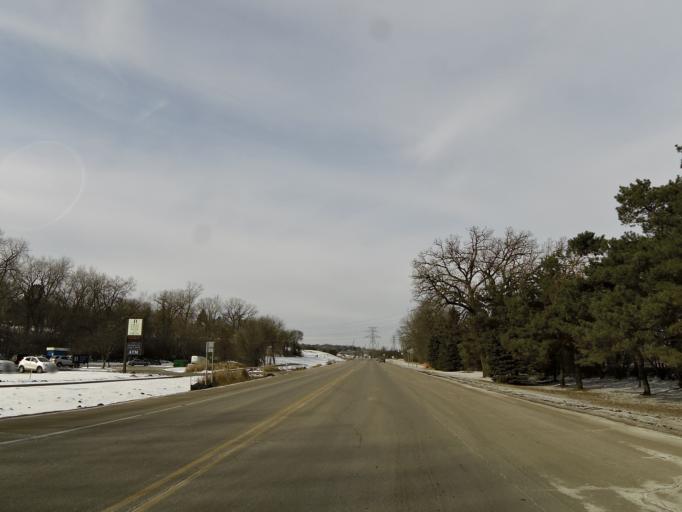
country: US
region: Minnesota
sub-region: Washington County
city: Bayport
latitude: 45.0261
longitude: -92.7833
